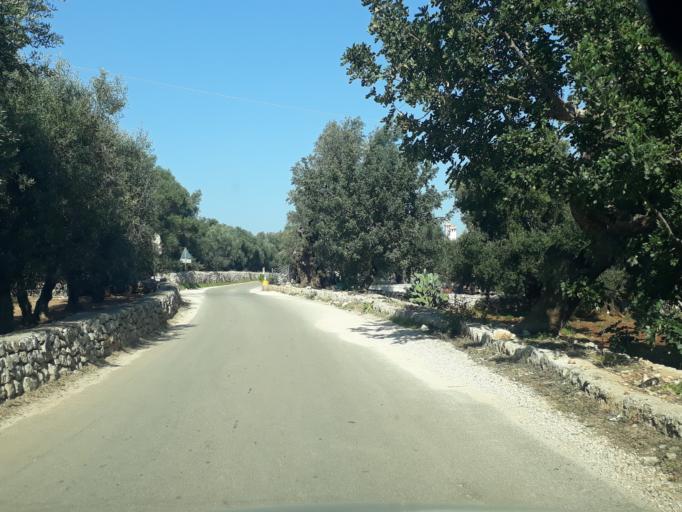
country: IT
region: Apulia
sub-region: Provincia di Brindisi
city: Fasano
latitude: 40.8405
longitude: 17.3465
